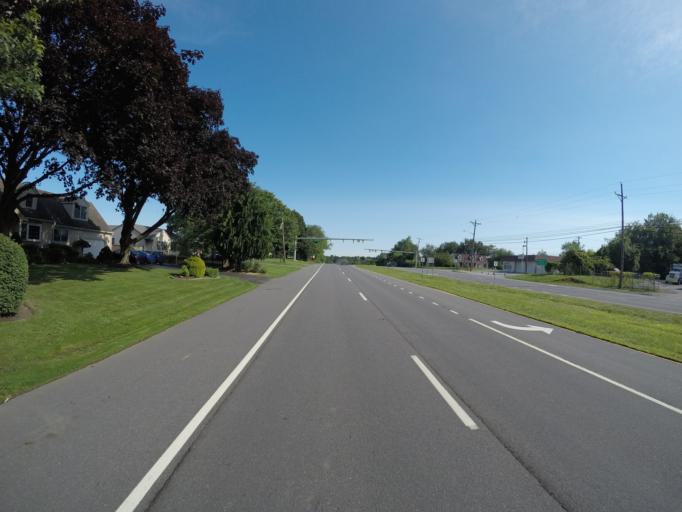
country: US
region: Delaware
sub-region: New Castle County
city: Bear
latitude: 39.5637
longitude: -75.6540
